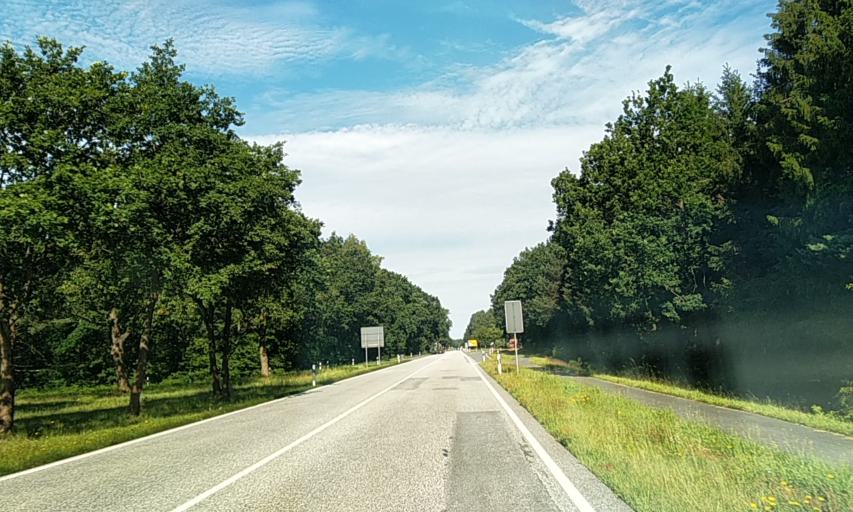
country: DE
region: Schleswig-Holstein
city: Owschlag
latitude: 54.3467
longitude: 9.5825
